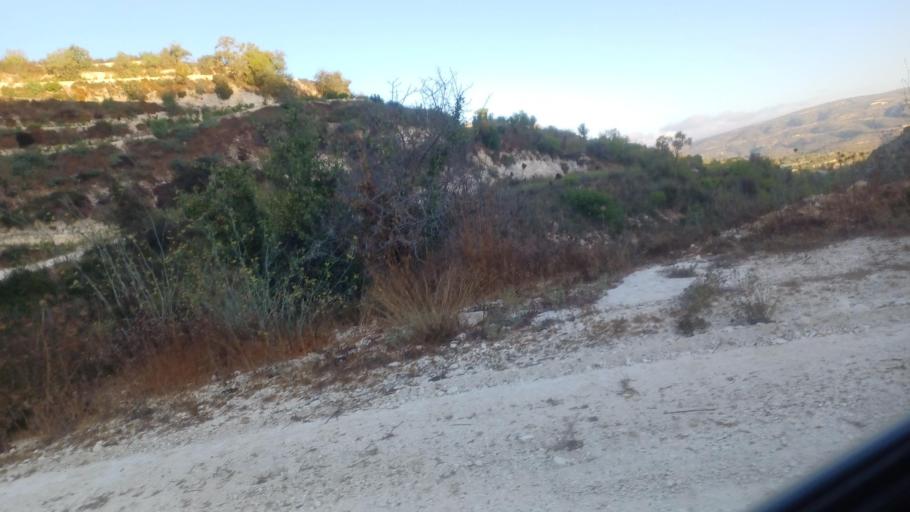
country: CY
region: Pafos
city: Tala
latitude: 34.8557
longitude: 32.4683
